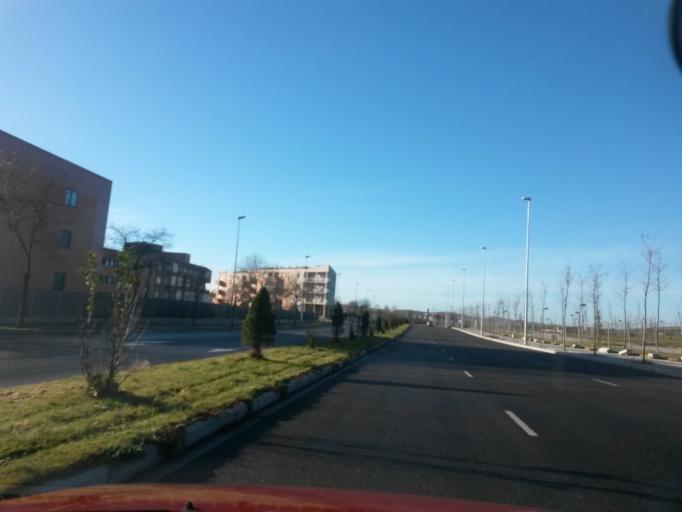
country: ES
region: Castille and Leon
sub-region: Provincia de Salamanca
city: Salamanca
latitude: 40.9693
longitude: -5.6849
